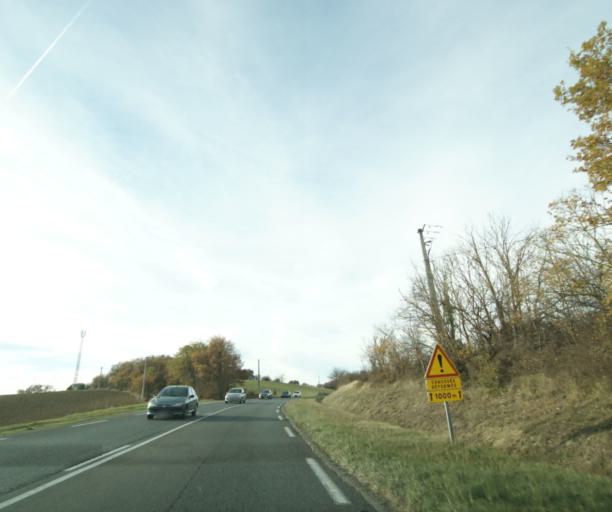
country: FR
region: Midi-Pyrenees
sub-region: Departement du Gers
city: Gimont
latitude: 43.6086
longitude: 0.9629
